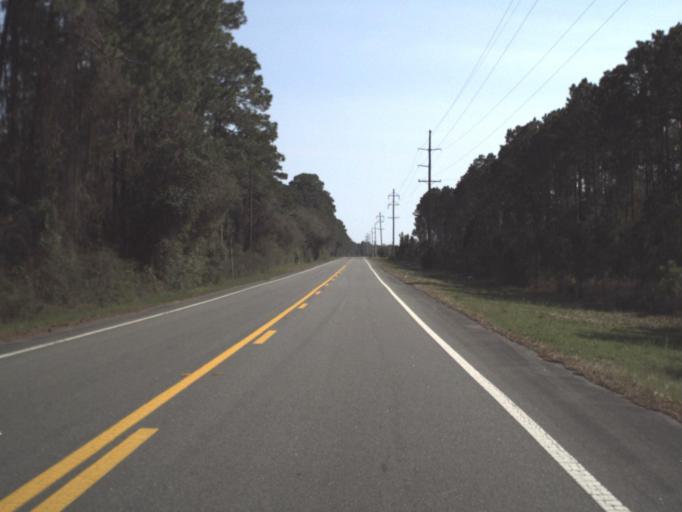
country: US
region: Florida
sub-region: Franklin County
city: Carrabelle
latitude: 29.9539
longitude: -84.5048
